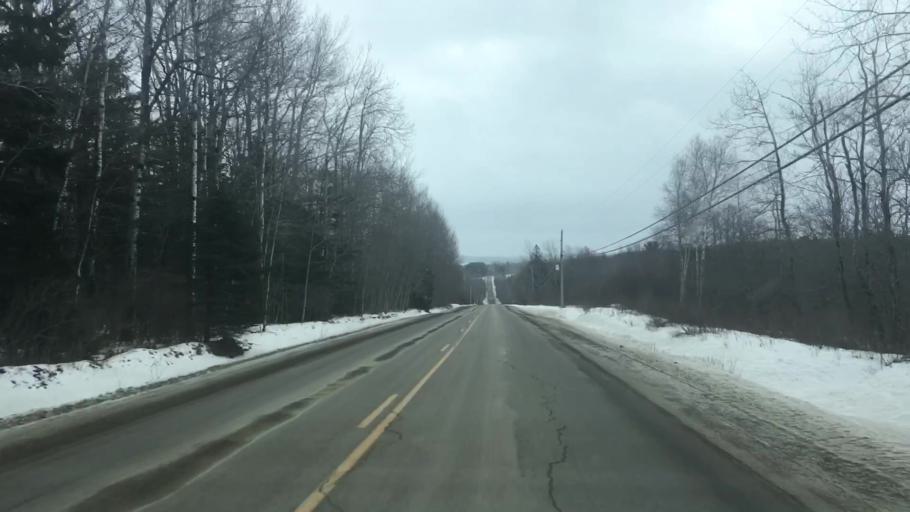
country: US
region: Maine
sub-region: Washington County
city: East Machias
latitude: 44.9736
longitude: -67.4496
